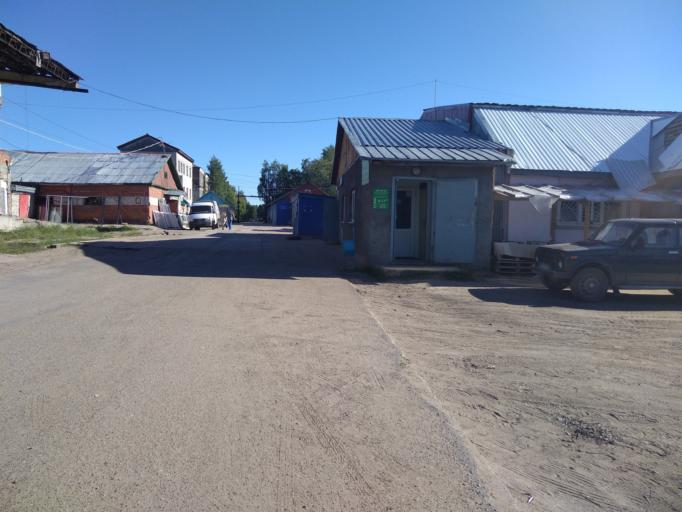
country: RU
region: Komi Republic
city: Pechora
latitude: 65.1213
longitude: 57.1655
